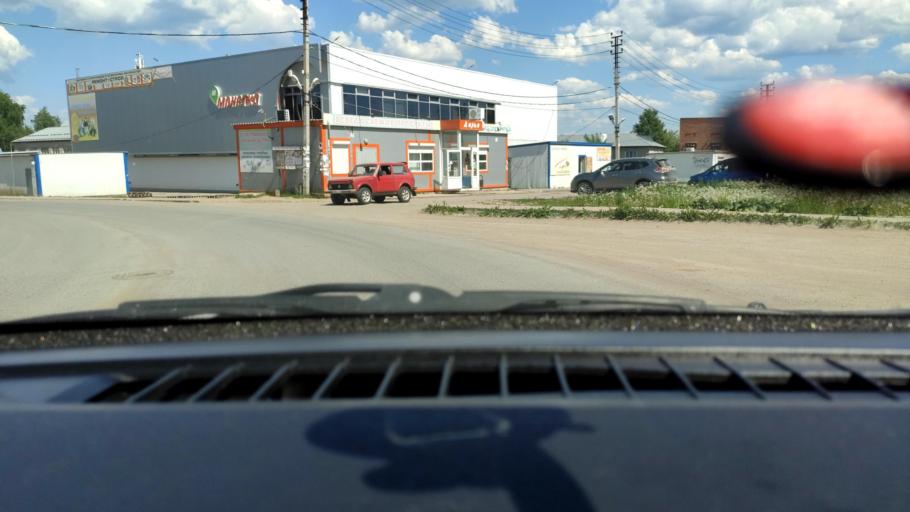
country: RU
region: Perm
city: Sylva
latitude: 58.0297
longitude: 56.7453
